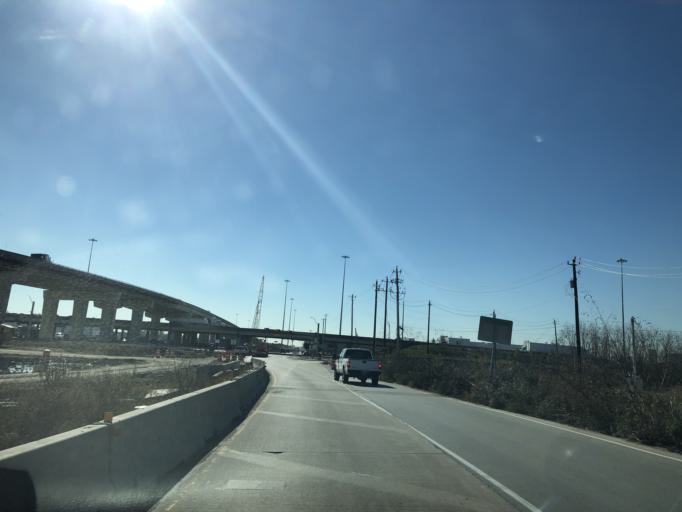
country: US
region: Texas
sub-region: Harris County
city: Deer Park
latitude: 29.7139
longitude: -95.1539
